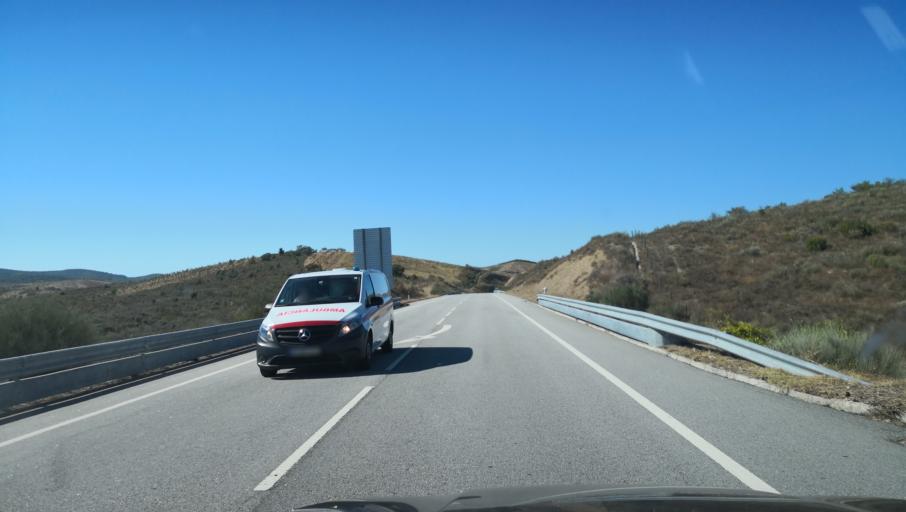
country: PT
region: Braganca
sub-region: Mirandela
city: Mirandela
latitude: 41.5188
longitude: -7.2329
